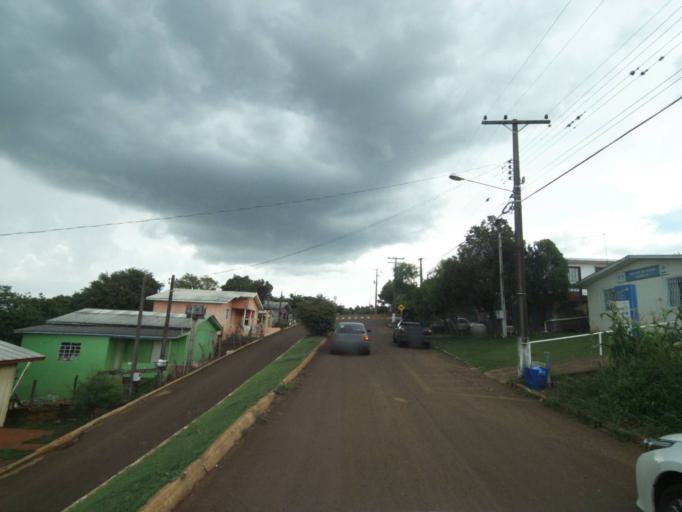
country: BR
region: Parana
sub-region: Guaraniacu
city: Guaraniacu
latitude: -25.0914
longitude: -52.8750
